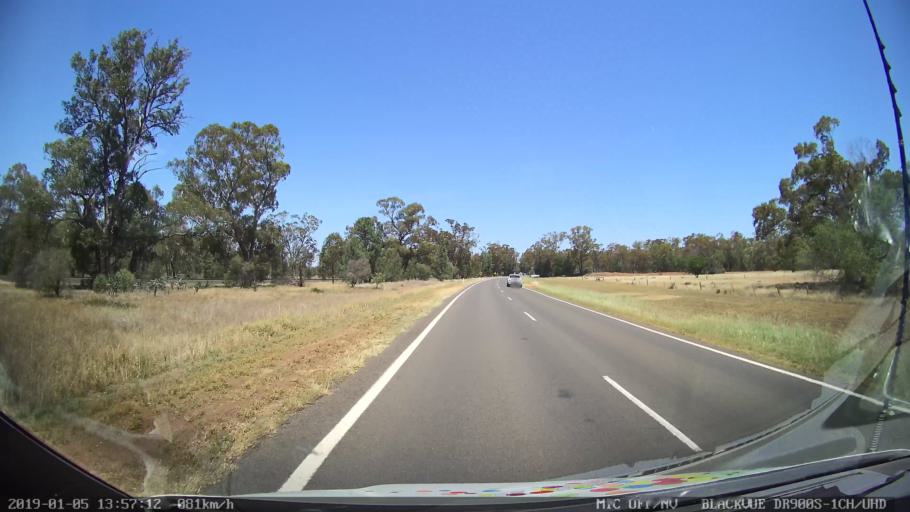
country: AU
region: New South Wales
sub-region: Gunnedah
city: Gunnedah
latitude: -31.1249
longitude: 150.2731
